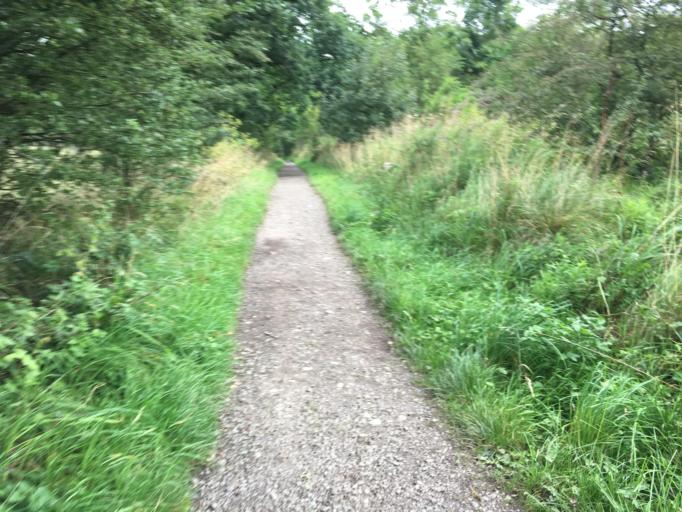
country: GB
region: Scotland
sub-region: Stirling
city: Killearn
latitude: 56.0400
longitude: -4.3946
